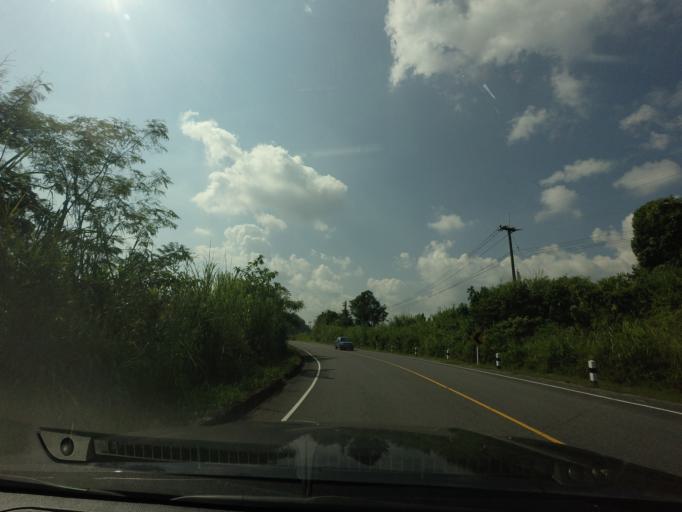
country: TH
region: Nan
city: Santi Suk
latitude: 18.9745
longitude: 101.0175
